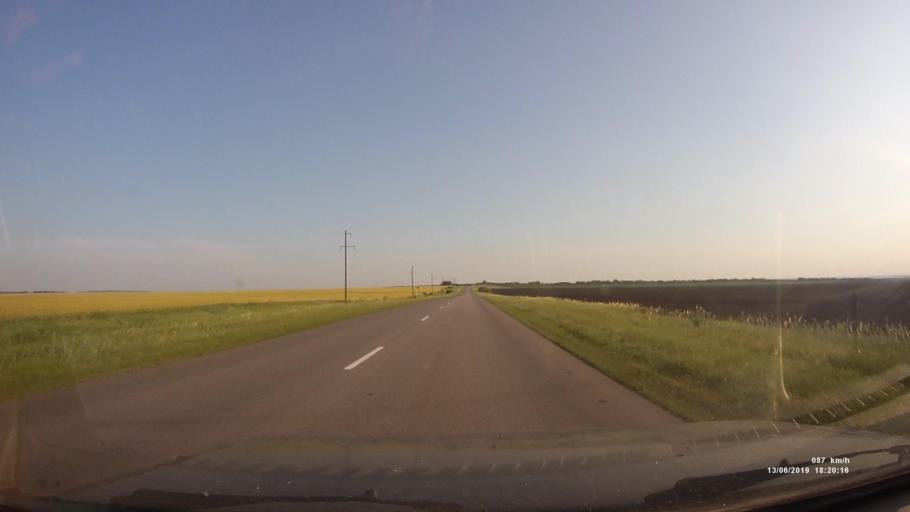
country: RU
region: Rostov
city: Kazanskaya
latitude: 49.8864
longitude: 41.3007
